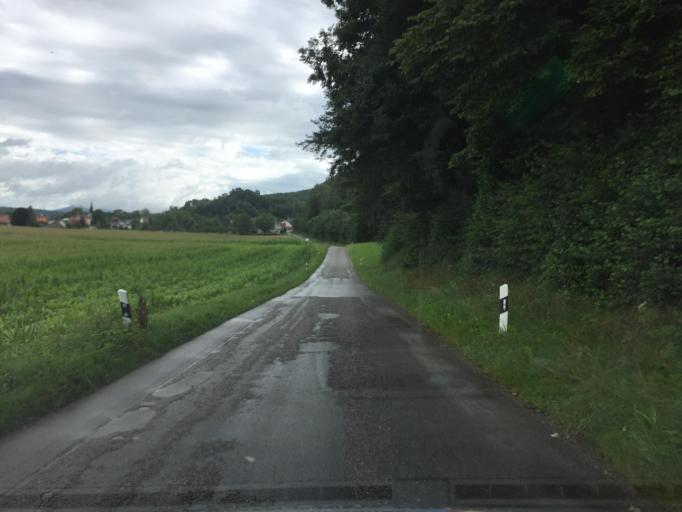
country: CH
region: Schaffhausen
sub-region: Bezirk Unterklettgau
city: Wilchingen
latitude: 47.6406
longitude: 8.4535
